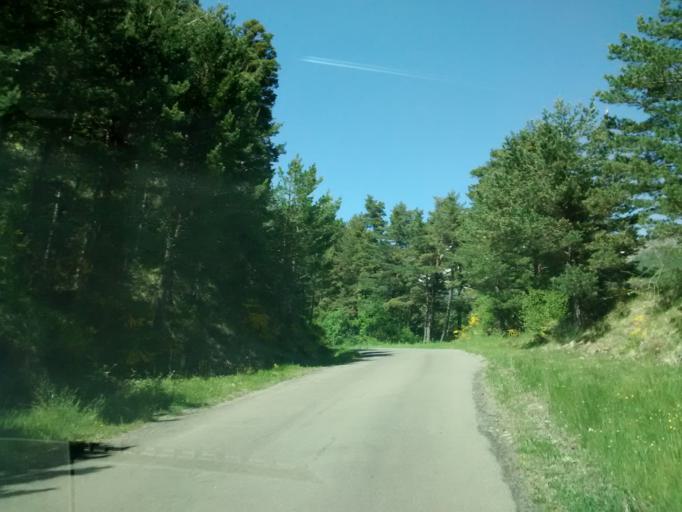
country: ES
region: Aragon
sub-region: Provincia de Huesca
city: Borau
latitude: 42.7161
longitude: -0.6049
